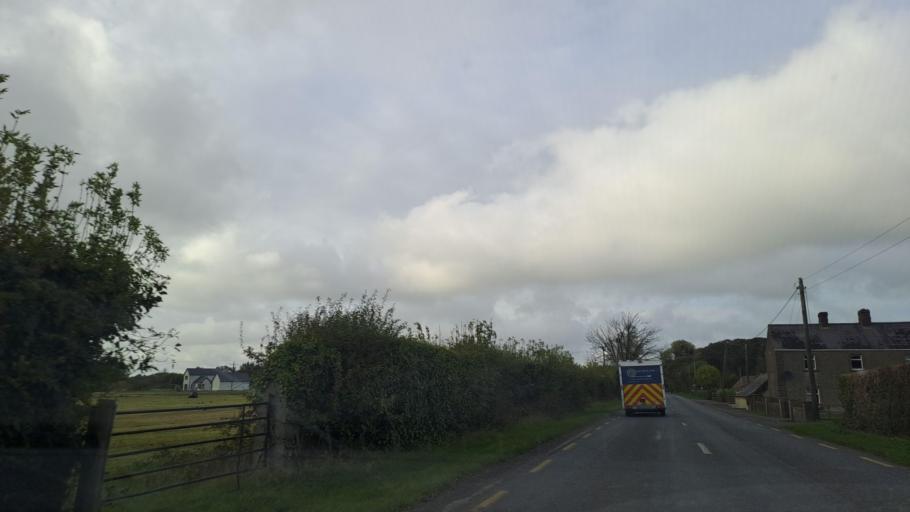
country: IE
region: Leinster
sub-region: An Mhi
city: Navan
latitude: 53.7409
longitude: -6.7150
